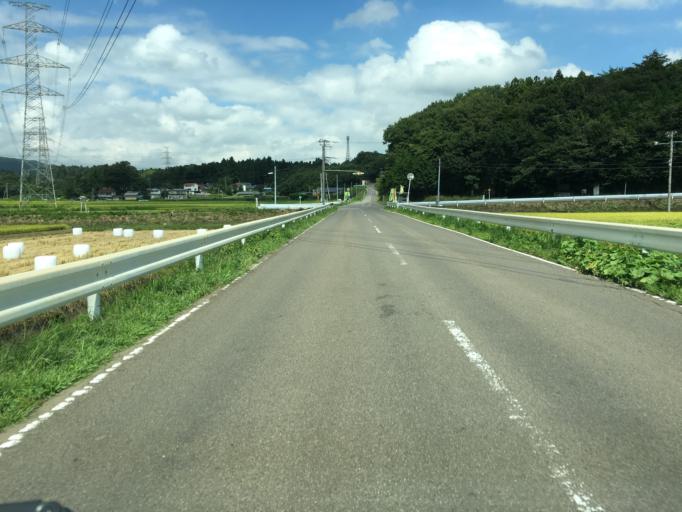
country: JP
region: Fukushima
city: Nihommatsu
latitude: 37.5664
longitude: 140.3843
